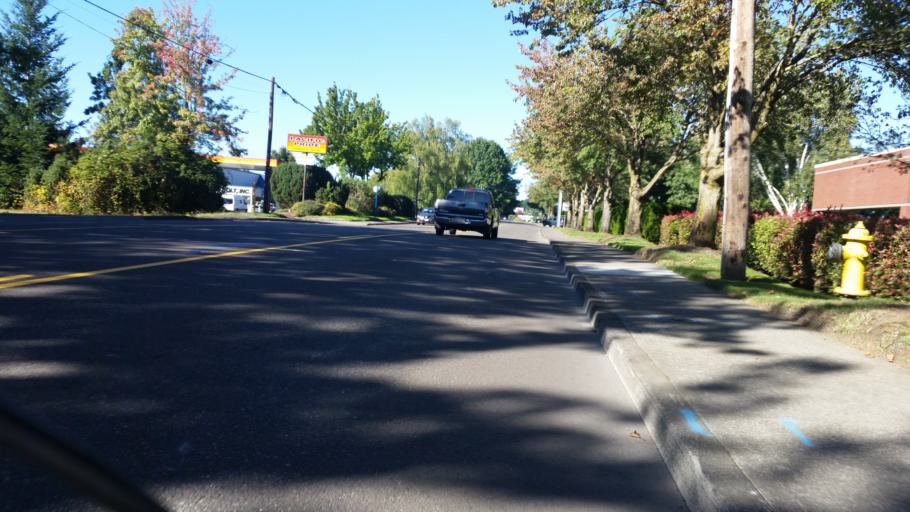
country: US
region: Oregon
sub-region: Washington County
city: Durham
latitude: 45.4107
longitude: -122.7490
